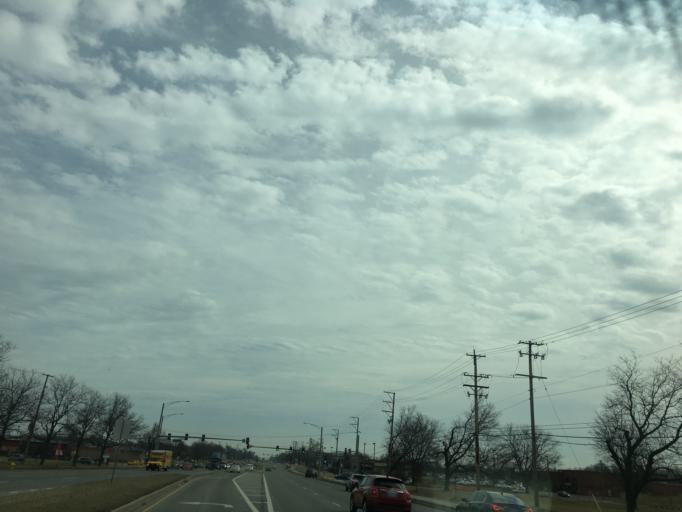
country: US
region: Illinois
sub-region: DuPage County
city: Woodridge
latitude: 41.7509
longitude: -88.0195
